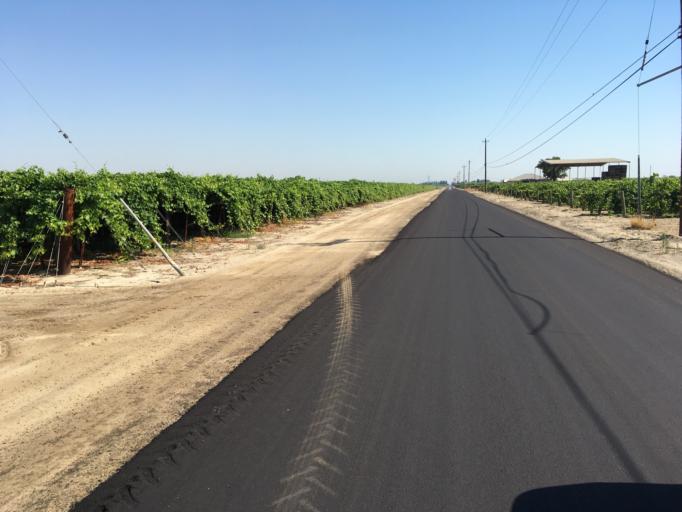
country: US
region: California
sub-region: Fresno County
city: Caruthers
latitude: 36.4965
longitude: -119.8091
